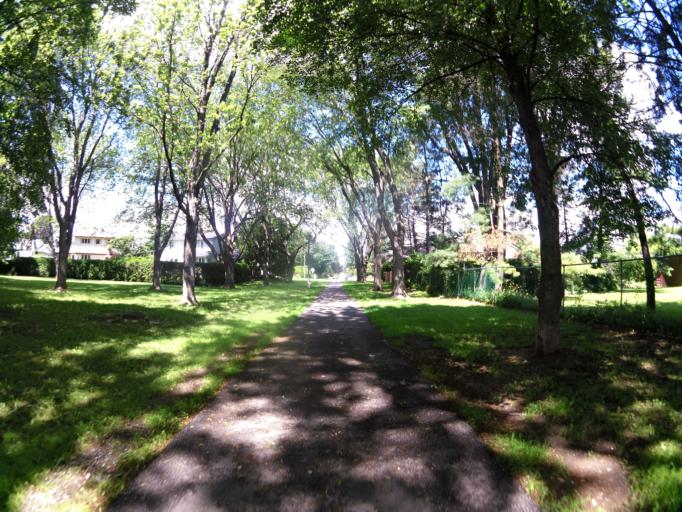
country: CA
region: Ontario
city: Ottawa
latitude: 45.3533
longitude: -75.7197
